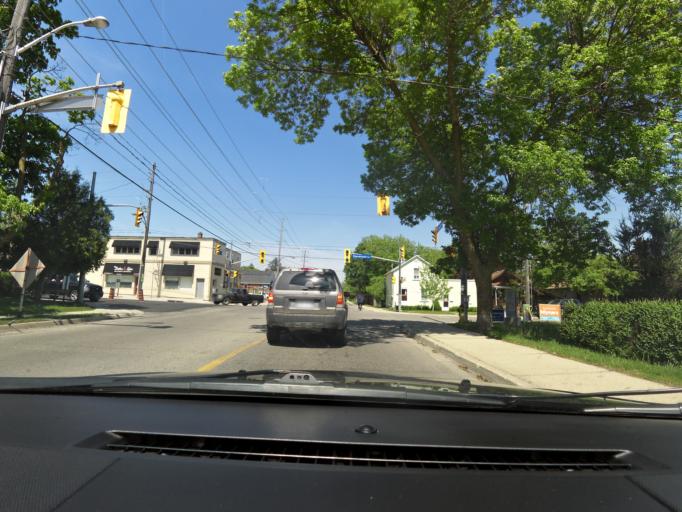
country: CA
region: Ontario
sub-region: Wellington County
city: Guelph
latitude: 43.5530
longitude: -80.2350
